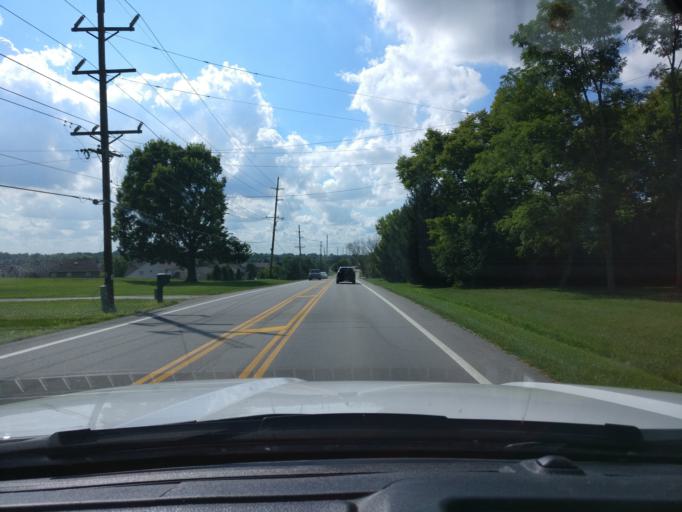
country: US
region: Ohio
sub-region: Warren County
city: Hunter
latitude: 39.4911
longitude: -84.2657
